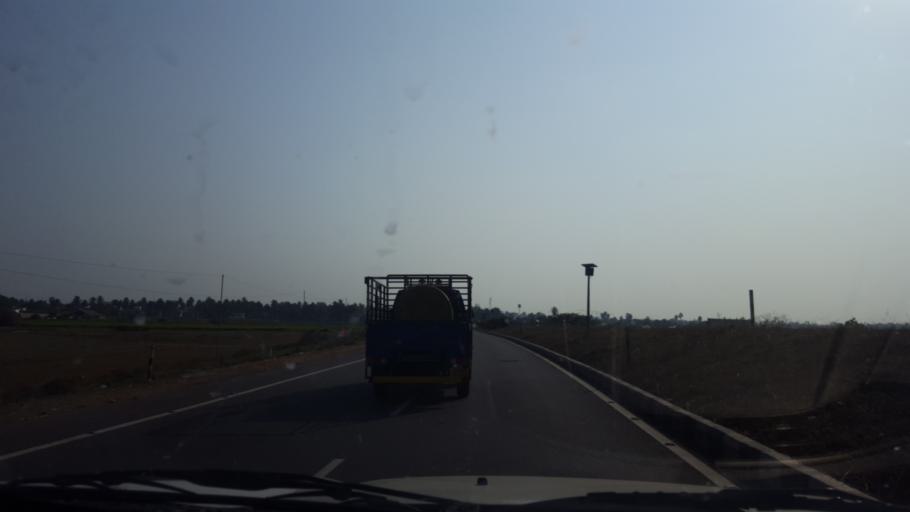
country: IN
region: Andhra Pradesh
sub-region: Vishakhapatnam
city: Etikoppaka
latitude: 17.4398
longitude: 82.7516
